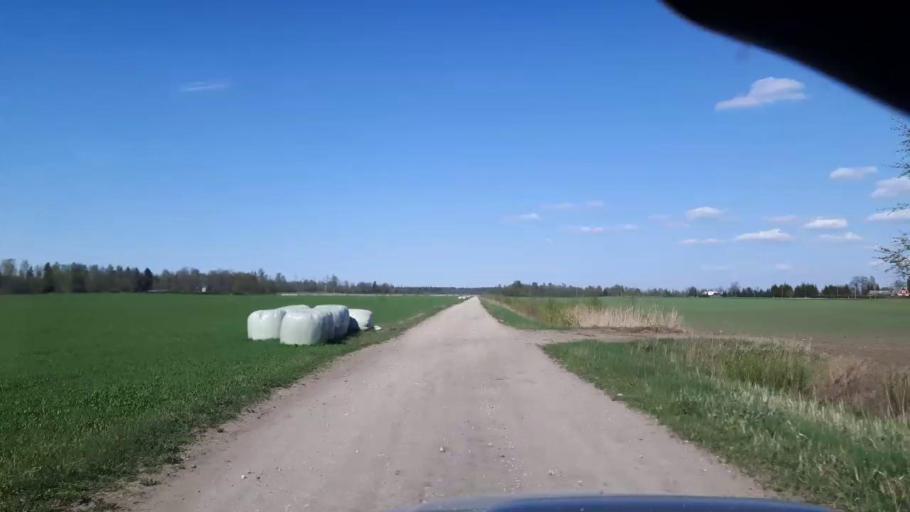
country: EE
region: Paernumaa
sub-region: Tootsi vald
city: Tootsi
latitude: 58.5271
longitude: 24.8236
